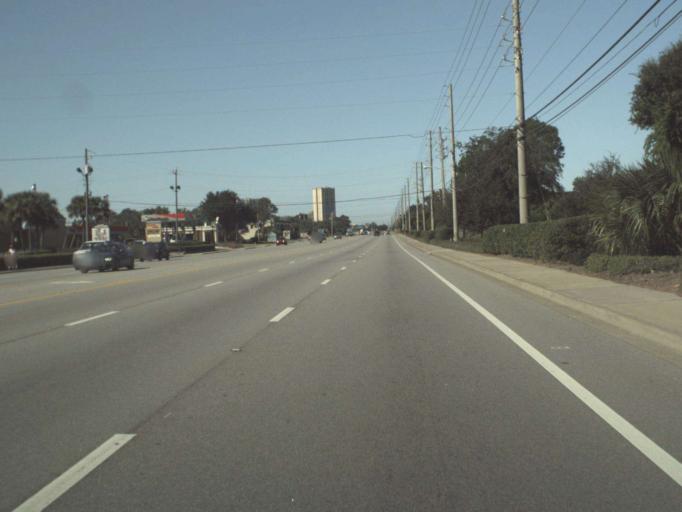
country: US
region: Florida
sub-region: Walton County
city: Miramar Beach
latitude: 30.3780
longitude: -86.3340
